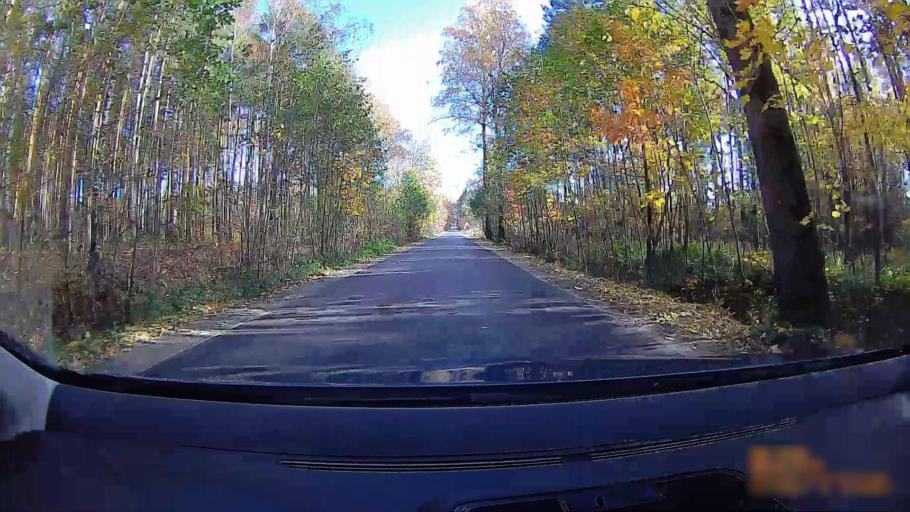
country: PL
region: Greater Poland Voivodeship
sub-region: Powiat ostrzeszowski
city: Doruchow
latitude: 51.4057
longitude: 18.0116
